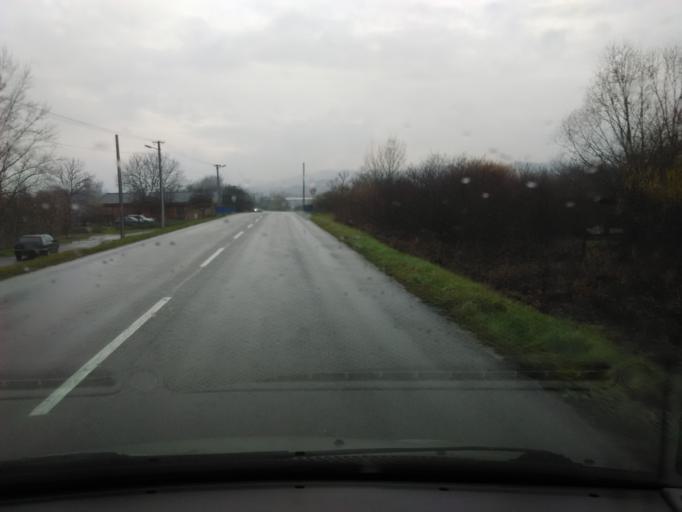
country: SK
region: Zilinsky
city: Bytca
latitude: 49.2183
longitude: 18.5483
